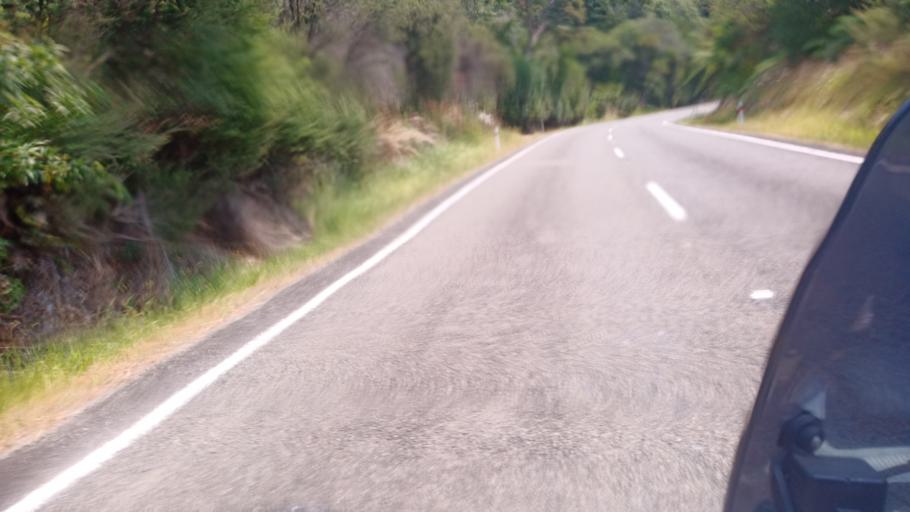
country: NZ
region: Bay of Plenty
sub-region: Opotiki District
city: Opotiki
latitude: -37.5765
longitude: 178.1090
